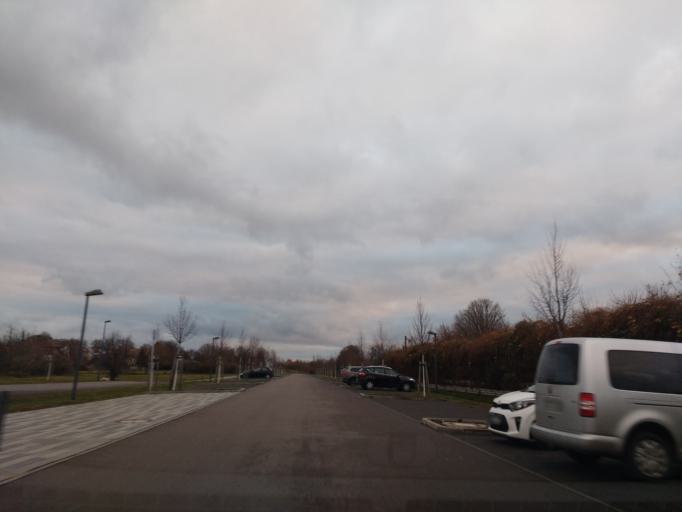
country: DE
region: Saxony-Anhalt
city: Krumpa
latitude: 51.2963
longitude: 11.8674
